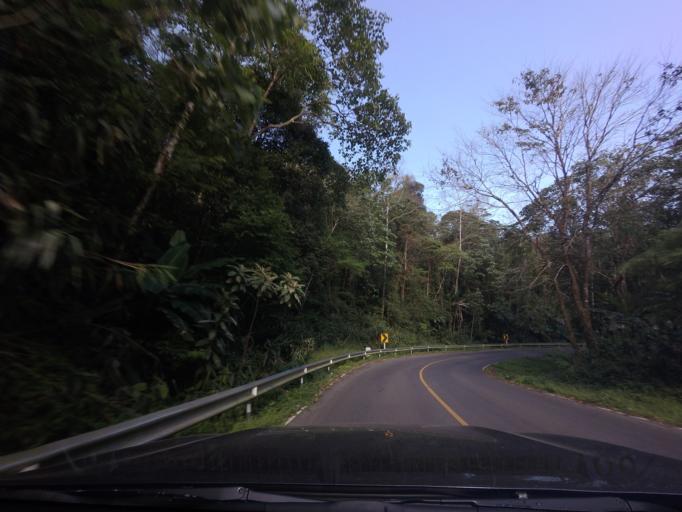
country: TH
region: Phetchabun
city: Lom Kao
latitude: 16.9305
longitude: 101.0711
